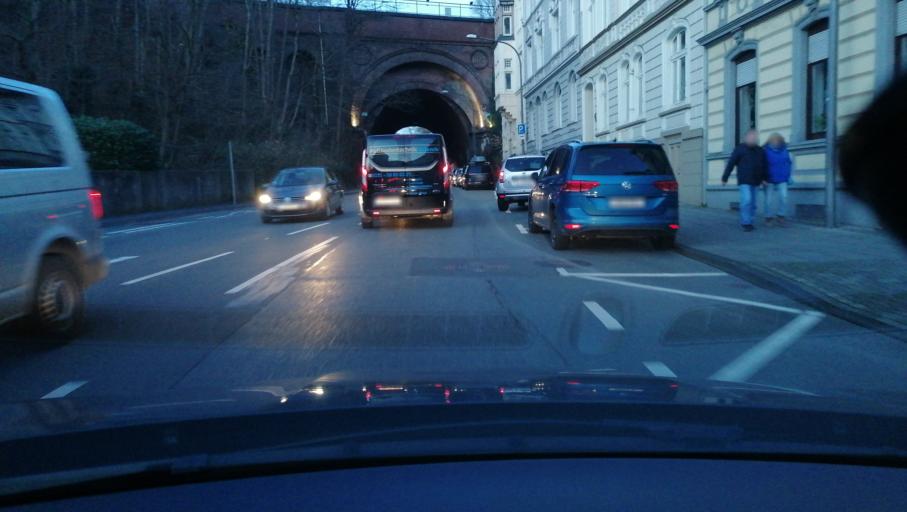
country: DE
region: North Rhine-Westphalia
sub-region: Regierungsbezirk Dusseldorf
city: Wuppertal
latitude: 51.2694
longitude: 7.1783
